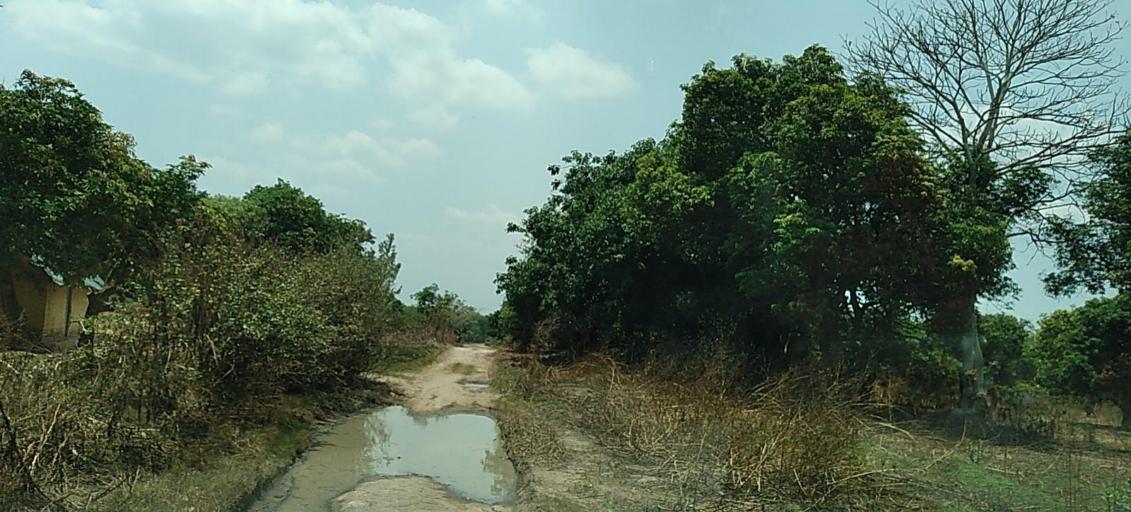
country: ZM
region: Copperbelt
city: Luanshya
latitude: -13.0957
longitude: 28.2888
